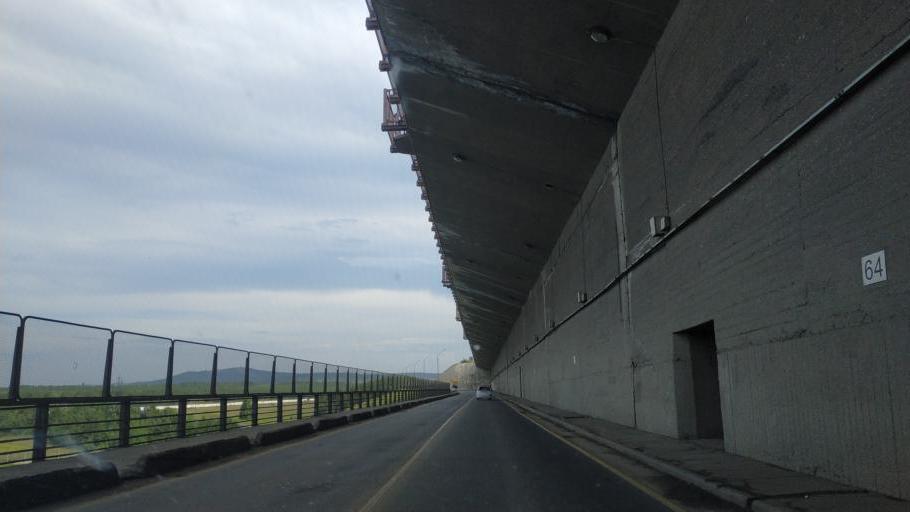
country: RU
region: Irkutsk
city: Bratsk
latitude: 56.2838
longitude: 101.7886
